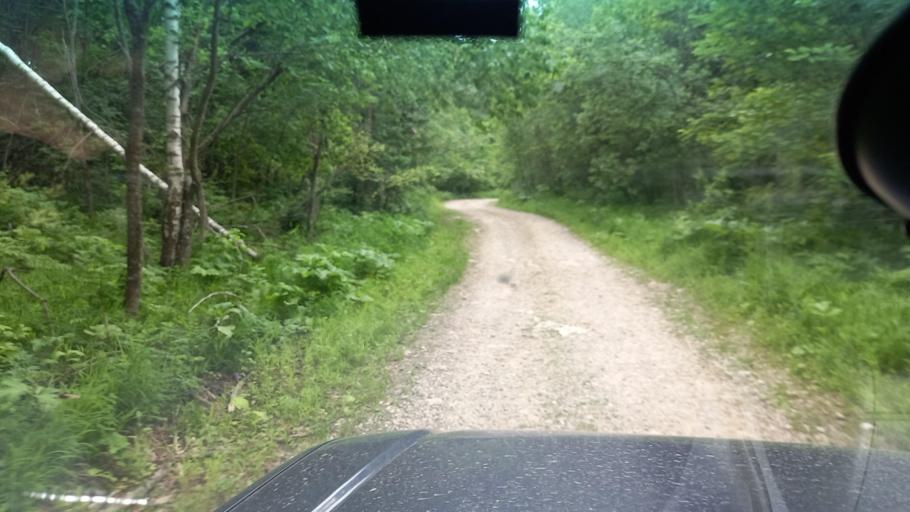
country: RU
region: Adygeya
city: Kamennomostskiy
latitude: 44.1479
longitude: 40.0478
